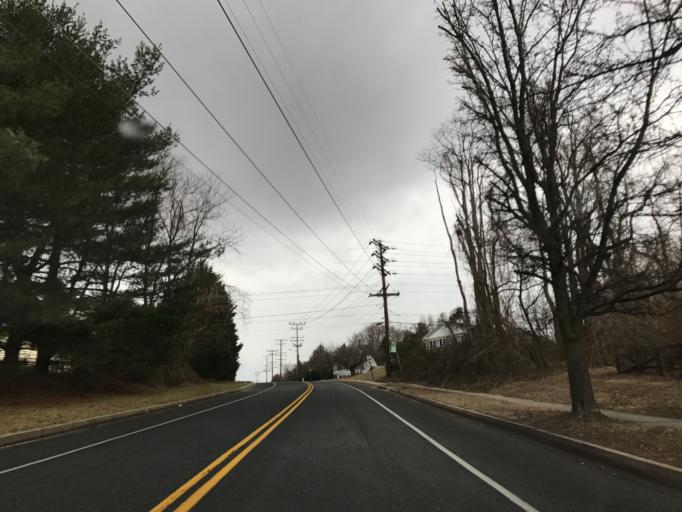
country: US
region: Maryland
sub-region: Harford County
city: South Bel Air
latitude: 39.5321
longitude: -76.3242
